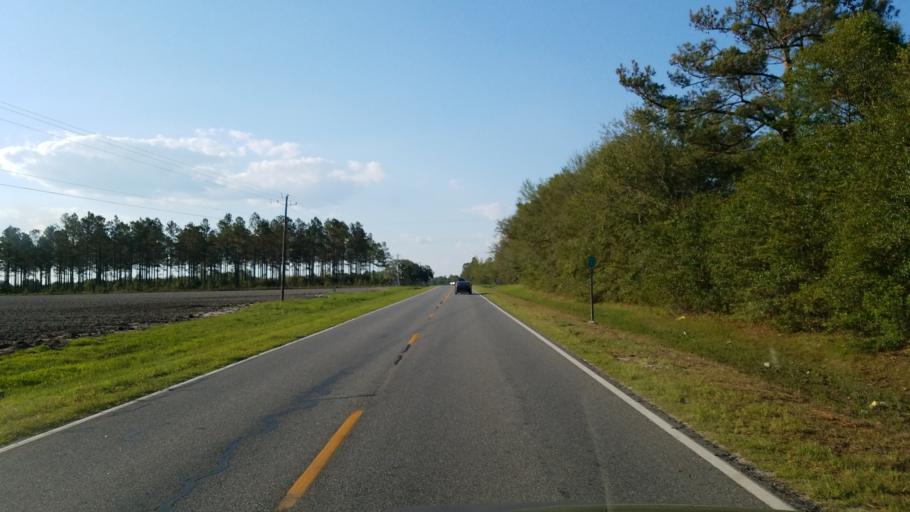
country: US
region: Georgia
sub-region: Lanier County
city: Lakeland
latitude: 31.0193
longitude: -83.0652
